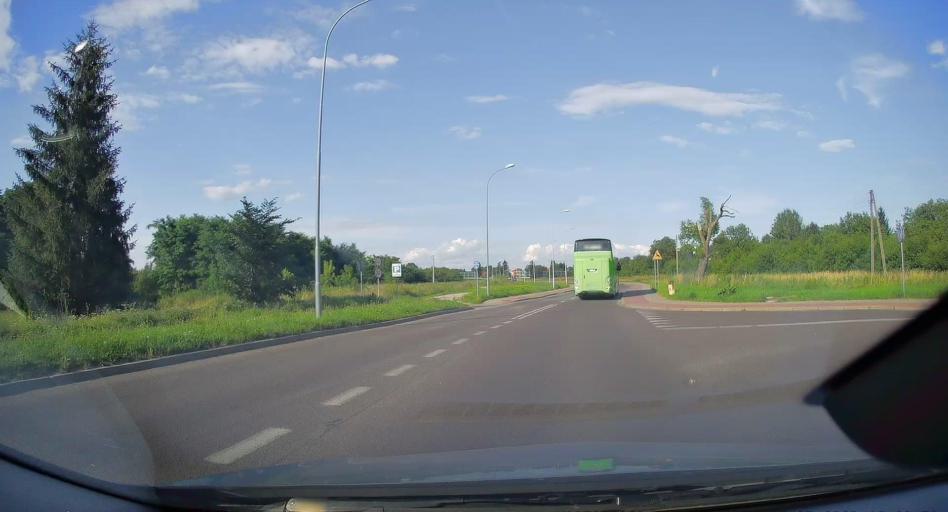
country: PL
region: Subcarpathian Voivodeship
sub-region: Przemysl
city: Przemysl
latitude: 49.7925
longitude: 22.7831
